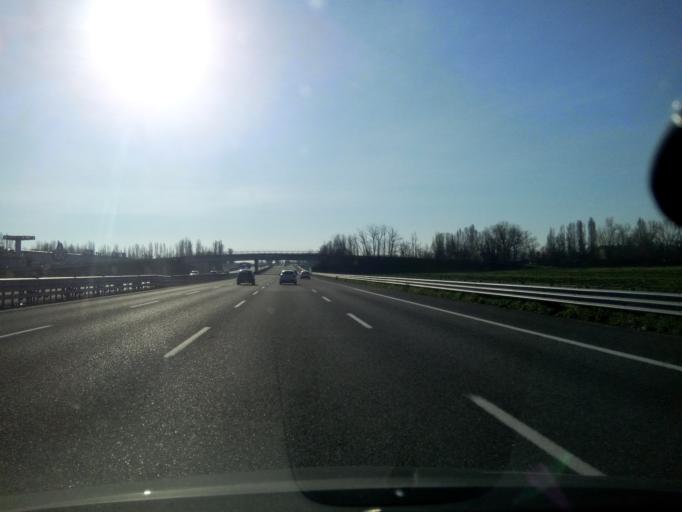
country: IT
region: Emilia-Romagna
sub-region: Provincia di Modena
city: San Damaso
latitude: 44.5847
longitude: 10.9637
